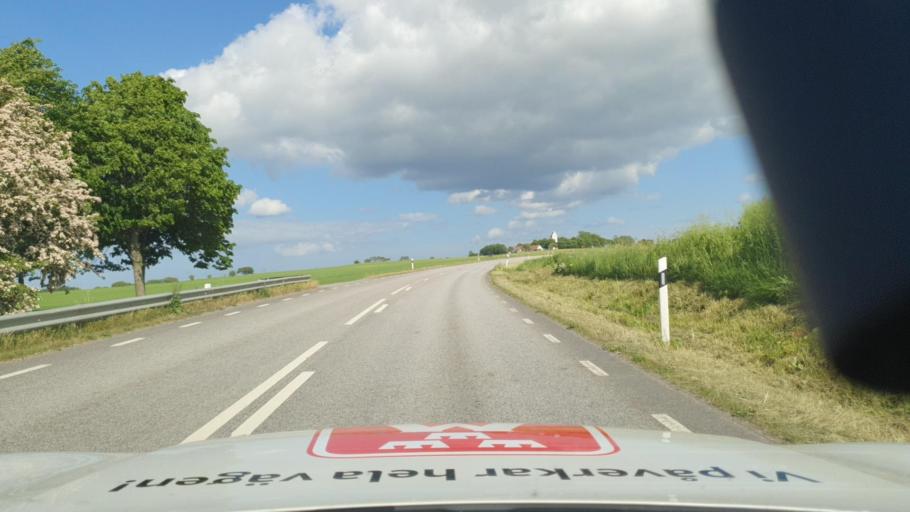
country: SE
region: Skane
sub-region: Simrishamns Kommun
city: Kivik
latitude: 55.5570
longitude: 14.1583
